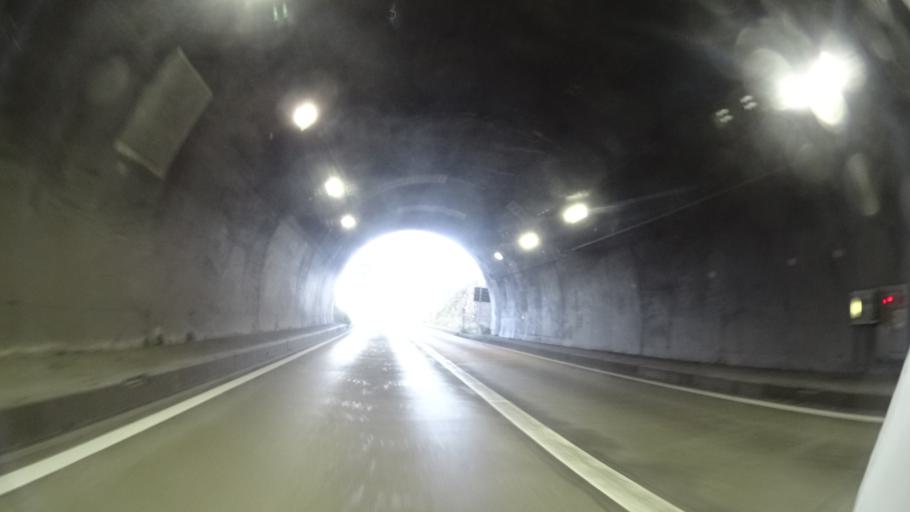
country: JP
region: Fukui
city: Tsuruga
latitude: 35.6732
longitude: 136.0883
